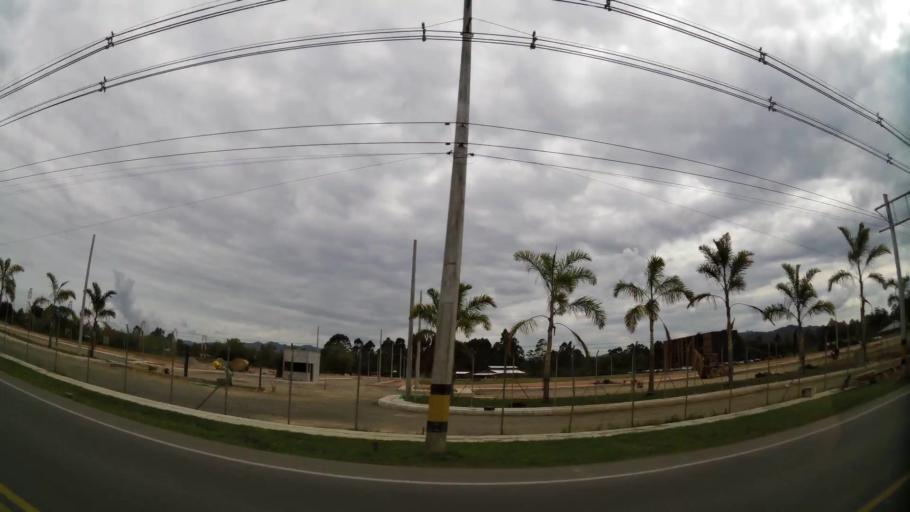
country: CO
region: Antioquia
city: Rionegro
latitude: 6.1465
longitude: -75.4253
